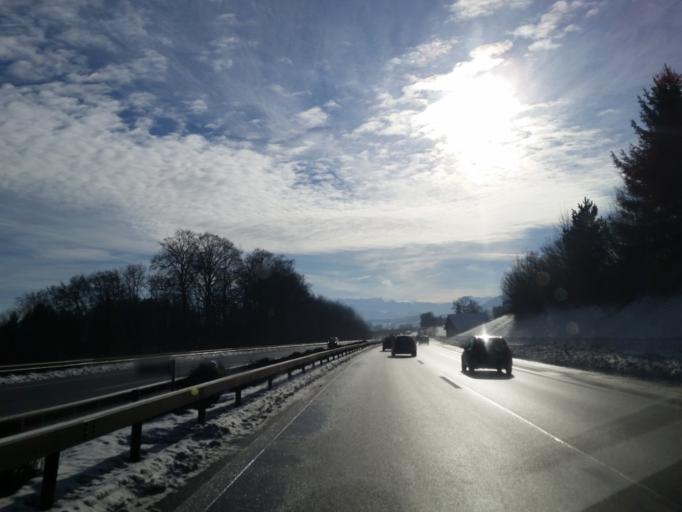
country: CH
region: Zurich
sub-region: Bezirk Horgen
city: Waedenswil / Hangenmoos
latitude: 47.2255
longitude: 8.6534
